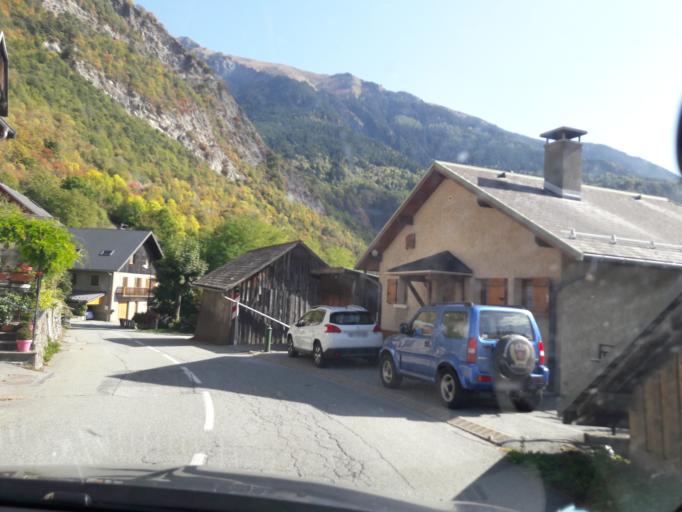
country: FR
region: Rhone-Alpes
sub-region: Departement de la Savoie
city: Saint-Jean-de-Maurienne
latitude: 45.3061
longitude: 6.3604
